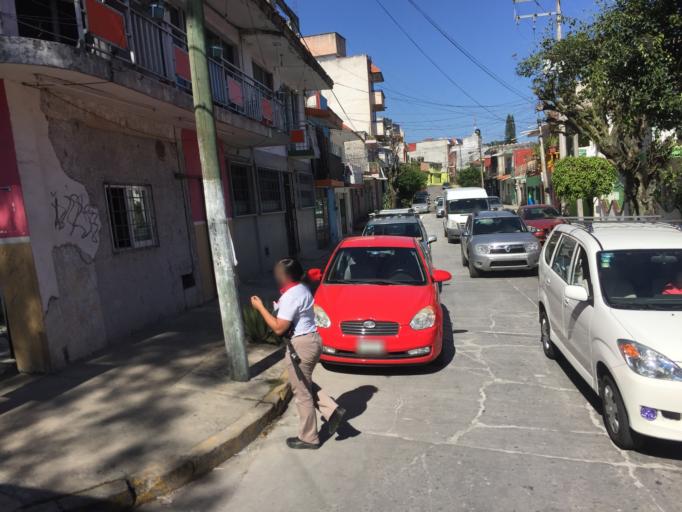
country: MX
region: Veracruz
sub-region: Xalapa
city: Xalapa de Enriquez
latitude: 19.5397
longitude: -96.9195
